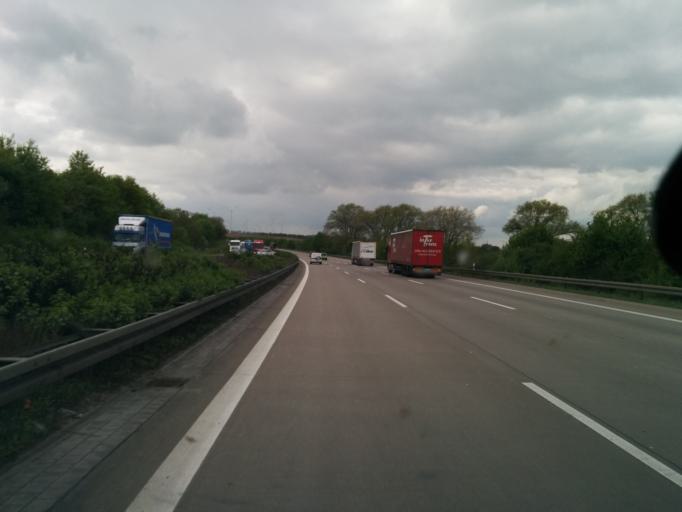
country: DE
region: Saxony-Anhalt
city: Gross Santersleben
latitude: 52.1879
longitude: 11.4386
